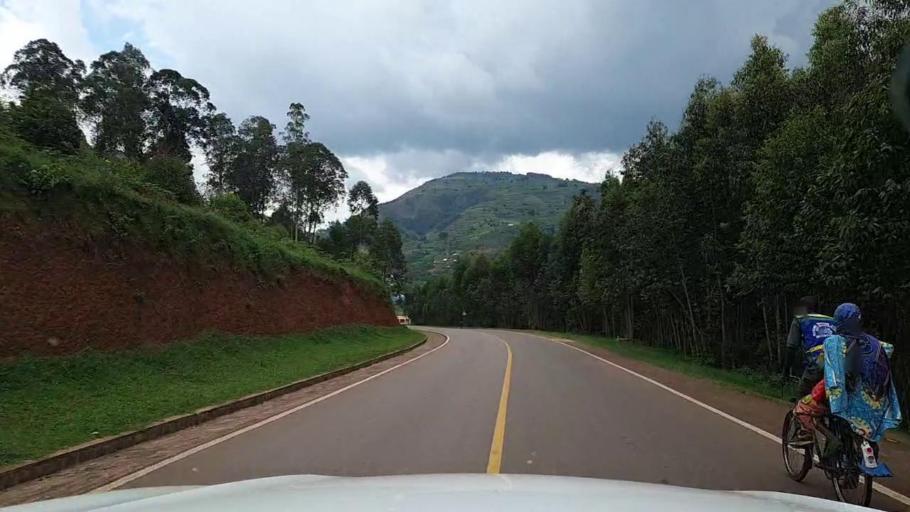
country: RW
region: Kigali
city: Kigali
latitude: -1.7731
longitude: 30.1254
